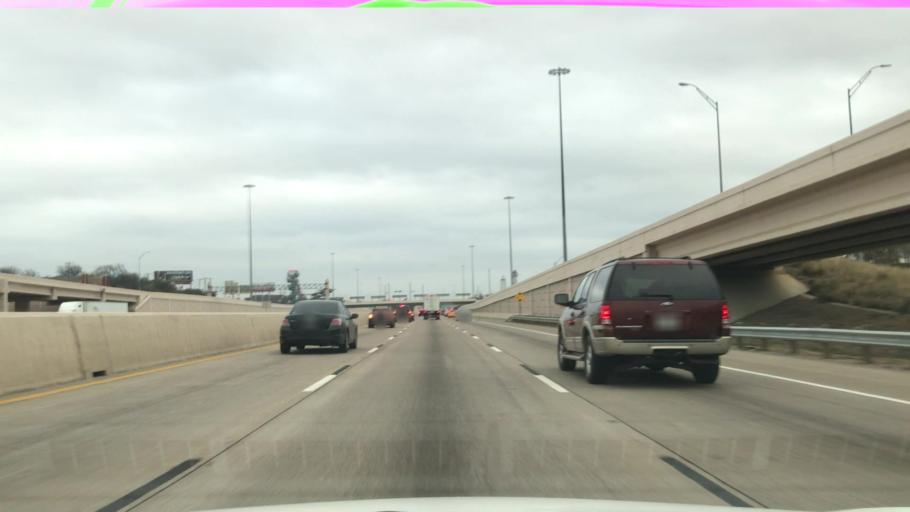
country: US
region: Texas
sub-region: Tarrant County
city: Arlington
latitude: 32.7595
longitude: -97.0912
